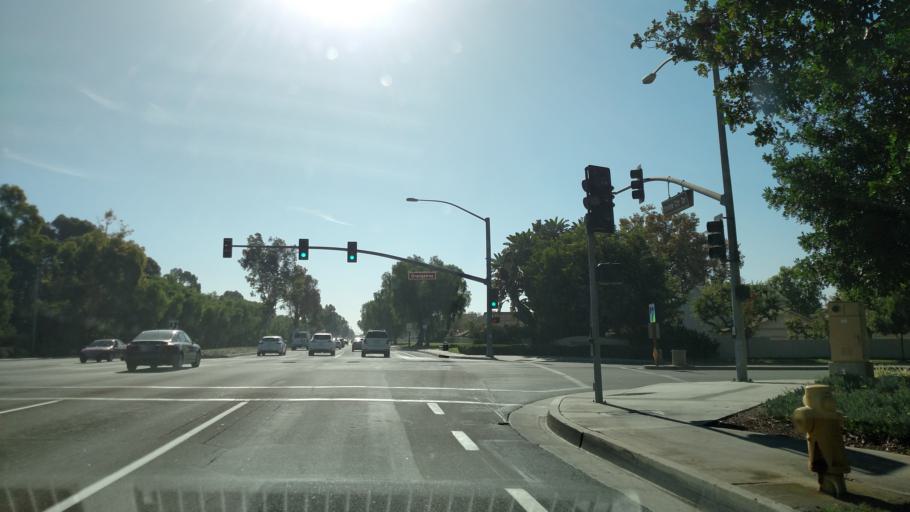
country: US
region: California
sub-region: Orange County
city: Irvine
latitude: 33.6750
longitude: -117.7724
